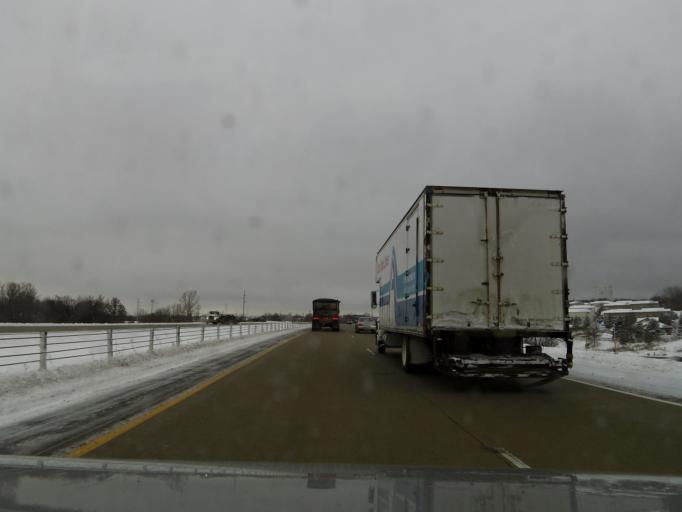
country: US
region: Minnesota
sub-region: Dakota County
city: Burnsville
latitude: 44.7604
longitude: -93.2455
